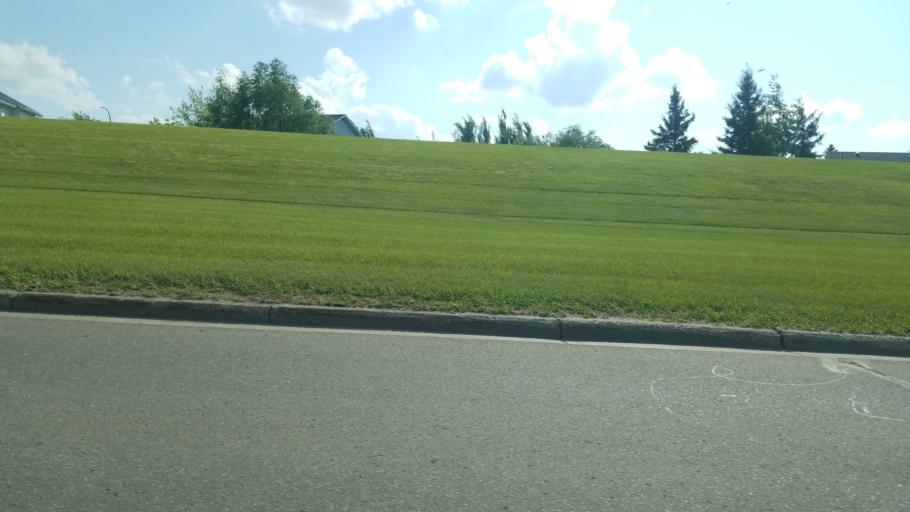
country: CA
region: Saskatchewan
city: Lloydminster
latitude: 53.2738
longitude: -110.0332
